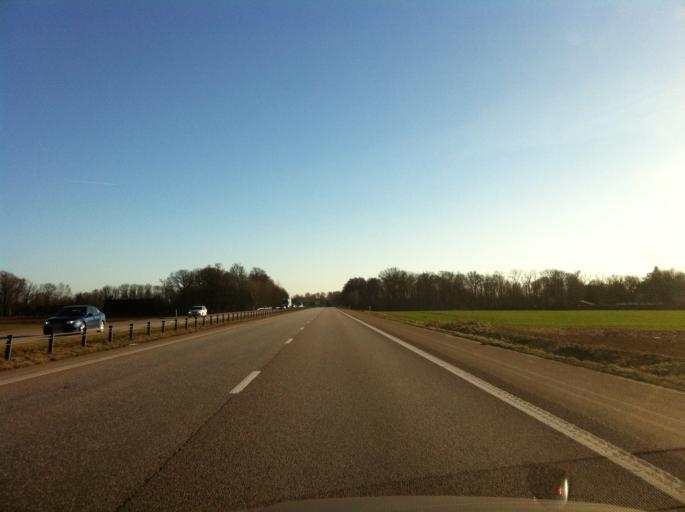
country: SE
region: Skane
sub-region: Angelholms Kommun
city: Strovelstorp
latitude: 56.1699
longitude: 12.8457
